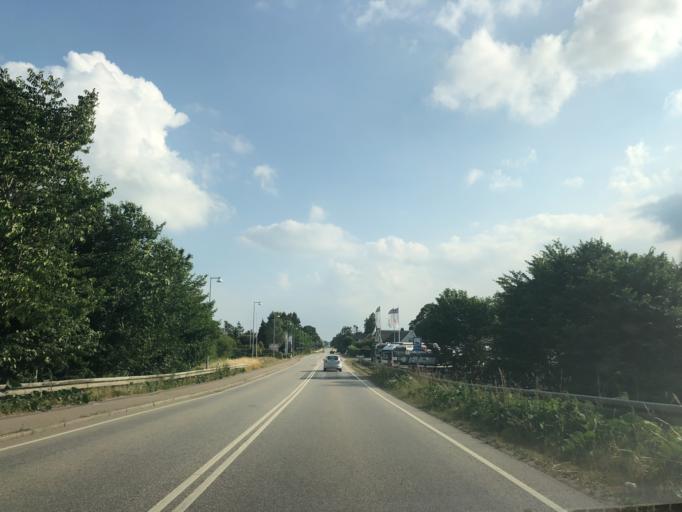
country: DK
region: Zealand
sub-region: Faxe Kommune
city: Ronnede
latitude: 55.3095
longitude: 12.0499
